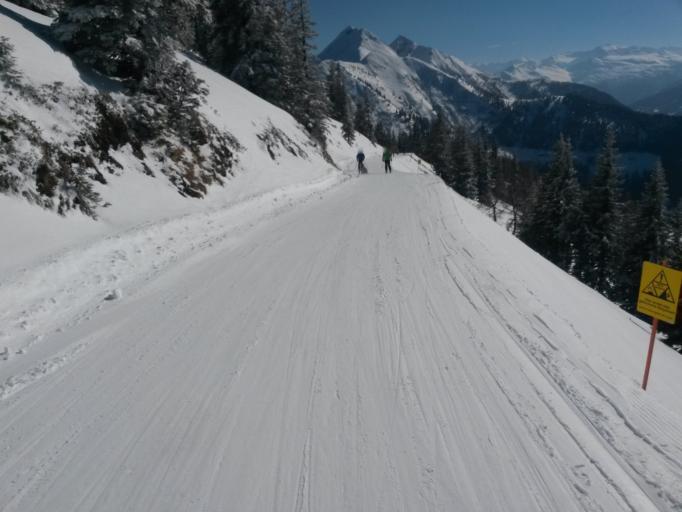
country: AT
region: Salzburg
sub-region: Politischer Bezirk Sankt Johann im Pongau
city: Dorfgastein
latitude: 47.2296
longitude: 13.1495
